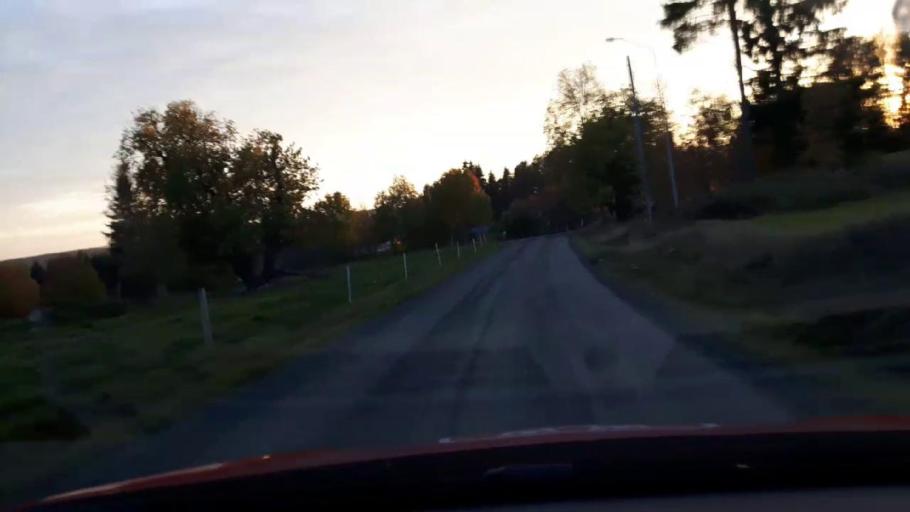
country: SE
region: Jaemtland
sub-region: OEstersunds Kommun
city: Lit
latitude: 63.2845
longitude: 14.7800
